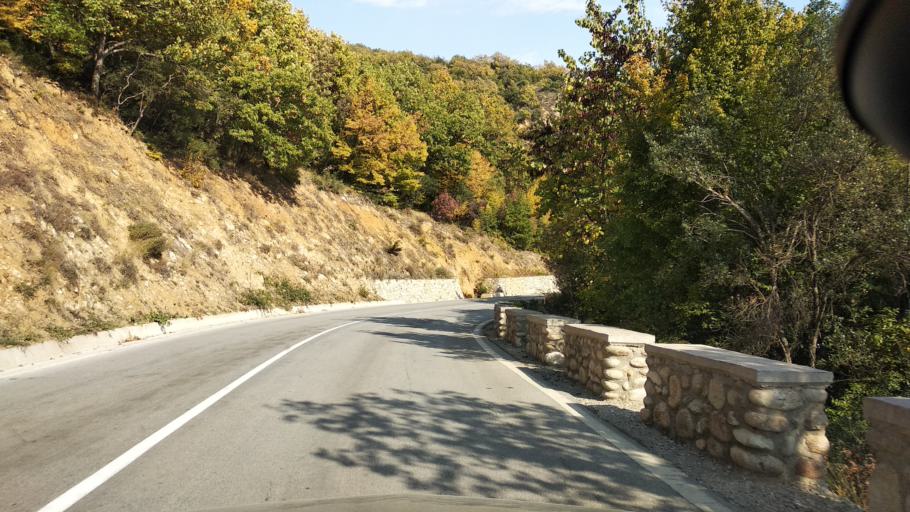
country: GR
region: Thessaly
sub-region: Trikala
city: Kastraki
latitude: 39.7268
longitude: 21.6360
